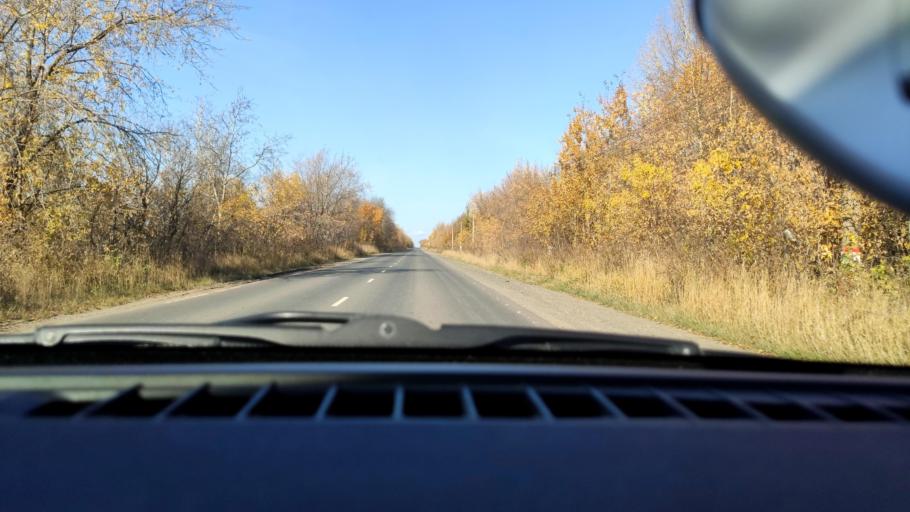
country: RU
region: Perm
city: Gamovo
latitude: 57.8994
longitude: 56.1792
